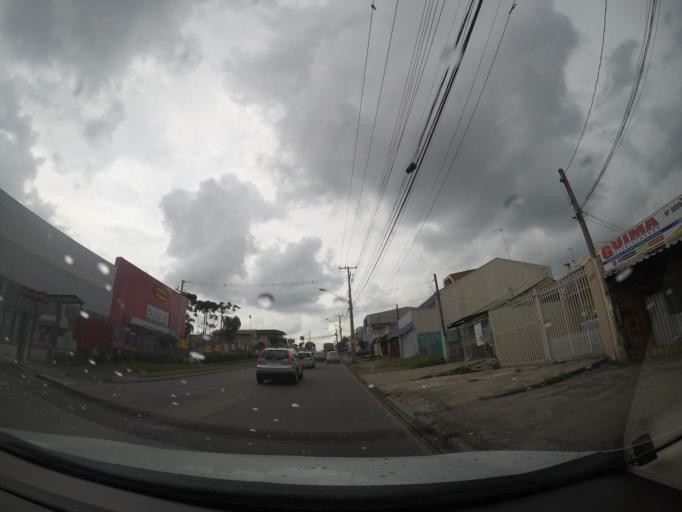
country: BR
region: Parana
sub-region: Sao Jose Dos Pinhais
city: Sao Jose dos Pinhais
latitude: -25.5240
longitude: -49.2450
